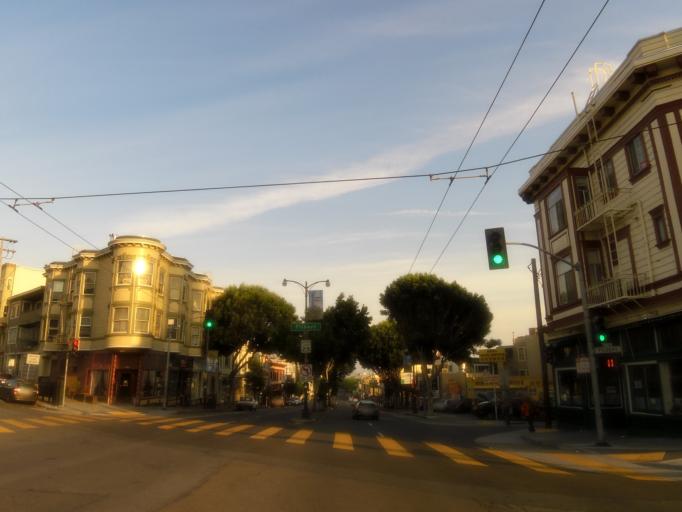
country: US
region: California
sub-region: San Francisco County
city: San Francisco
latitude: 37.8011
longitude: -122.4113
